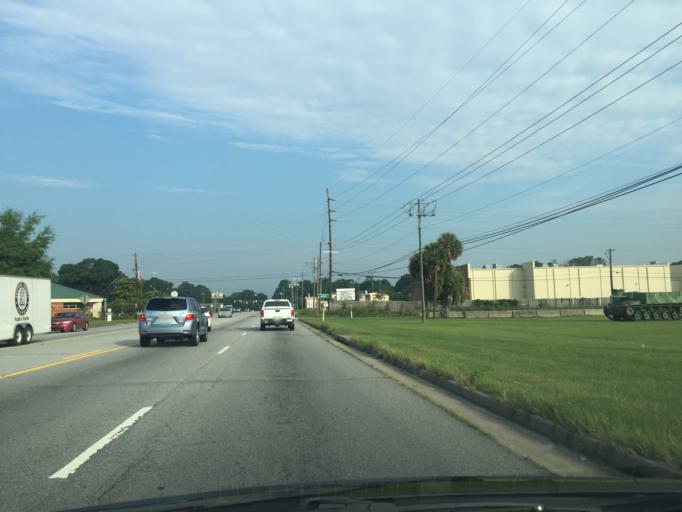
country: US
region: Georgia
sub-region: Chatham County
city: Isle of Hope
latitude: 32.0058
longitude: -81.0976
